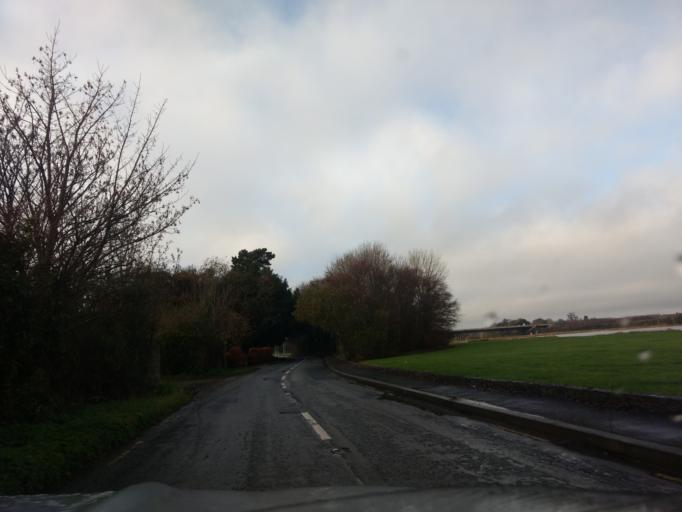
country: IE
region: Leinster
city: Kinsealy-Drinan
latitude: 53.4621
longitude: -6.1954
